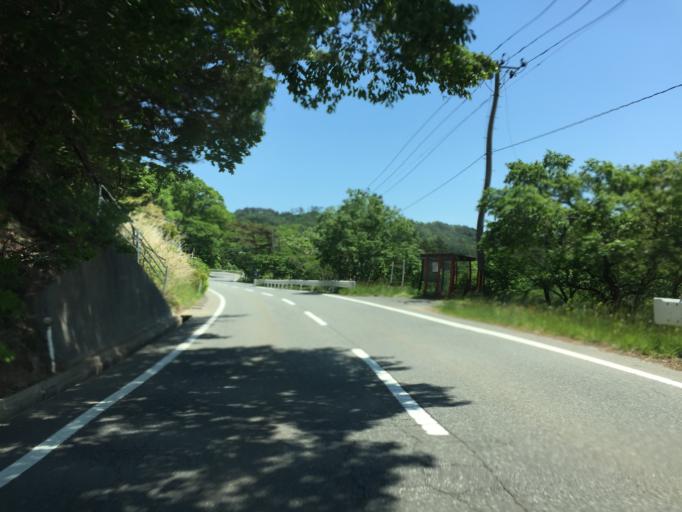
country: JP
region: Fukushima
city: Funehikimachi-funehiki
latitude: 37.5030
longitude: 140.7708
